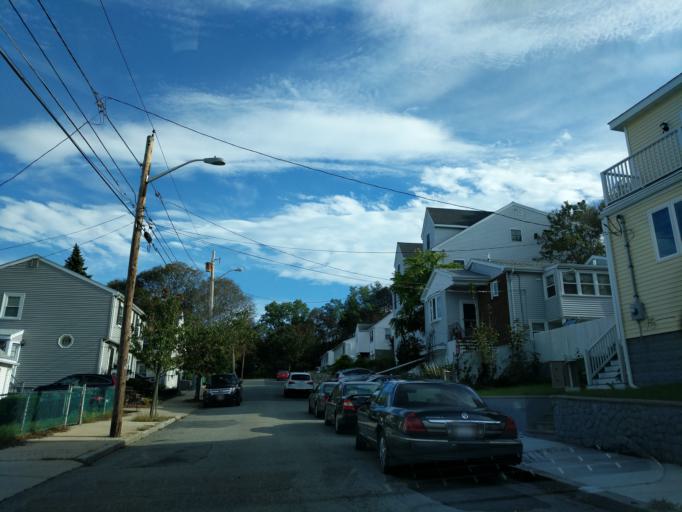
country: US
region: Massachusetts
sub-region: Middlesex County
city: Everett
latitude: 42.4104
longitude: -71.0367
